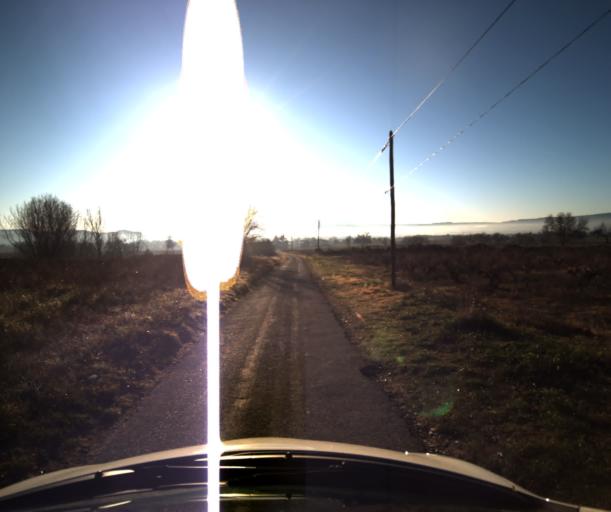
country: FR
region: Provence-Alpes-Cote d'Azur
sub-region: Departement du Vaucluse
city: Pertuis
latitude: 43.7067
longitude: 5.4873
